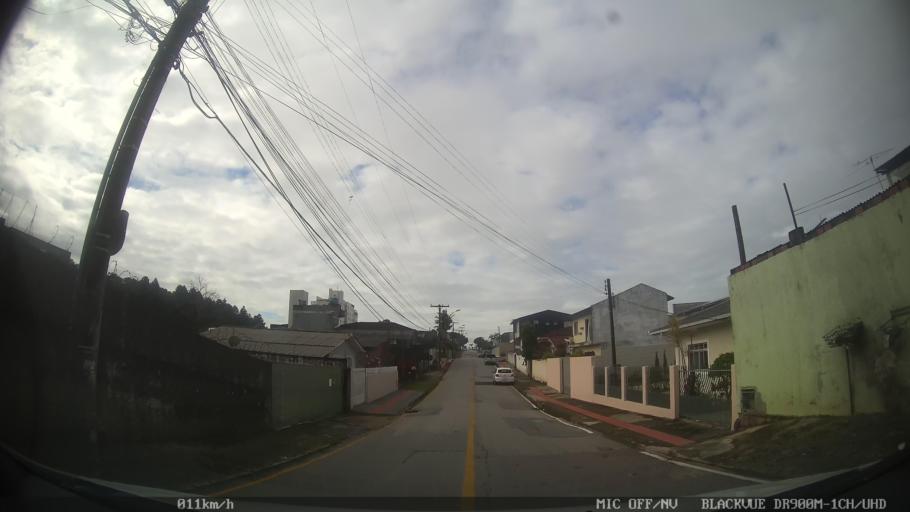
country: BR
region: Santa Catarina
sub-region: Sao Jose
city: Campinas
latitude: -27.5430
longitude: -48.6241
